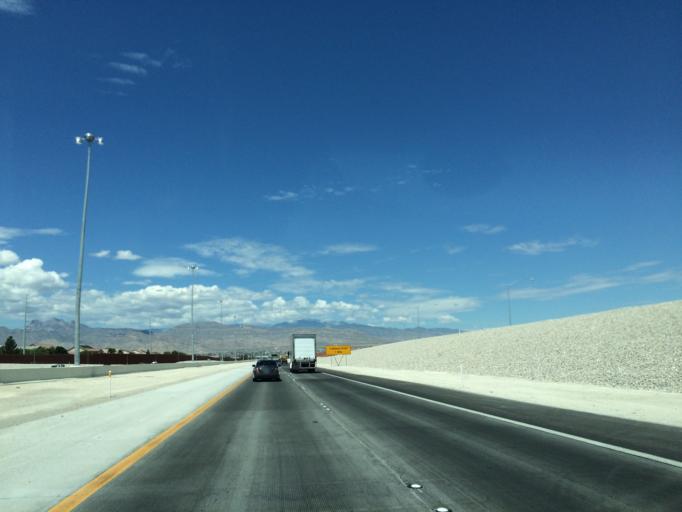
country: US
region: Nevada
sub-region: Clark County
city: North Las Vegas
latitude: 36.2754
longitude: -115.2253
